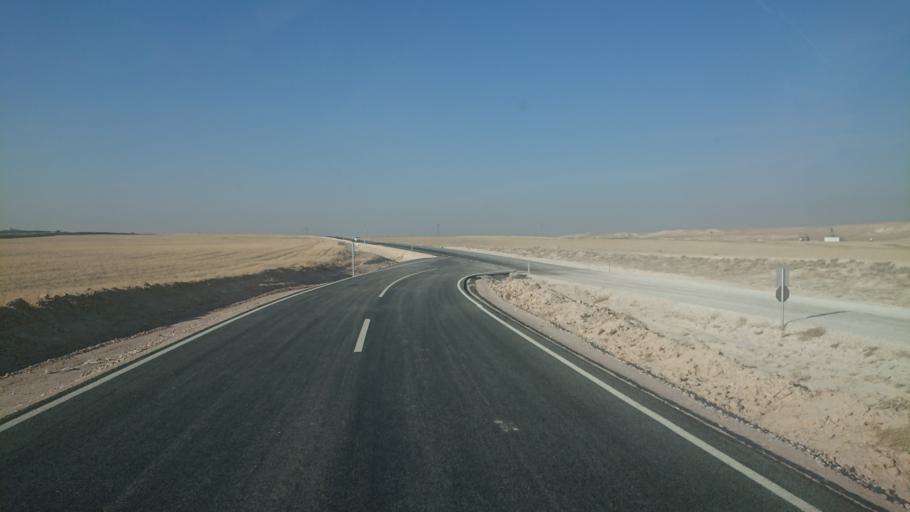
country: TR
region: Aksaray
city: Sultanhani
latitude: 38.0852
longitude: 33.6146
